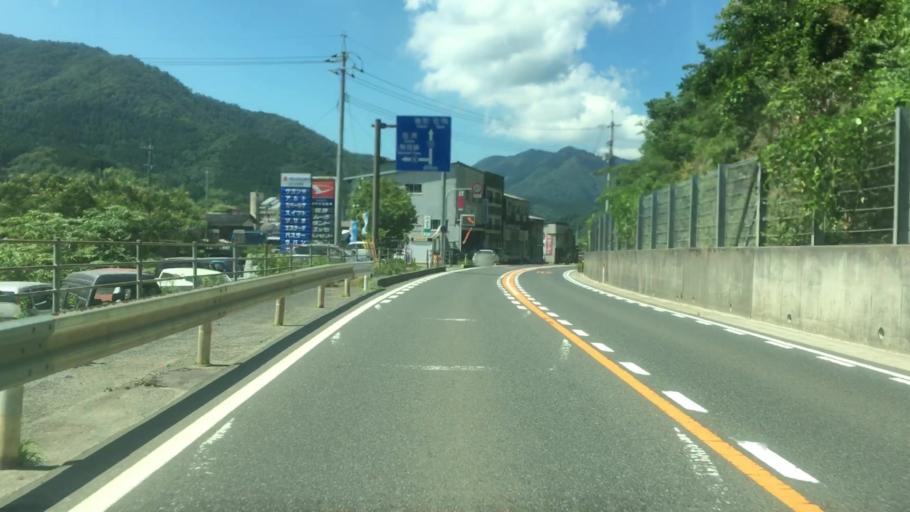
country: JP
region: Tottori
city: Tottori
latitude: 35.2595
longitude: 134.2276
